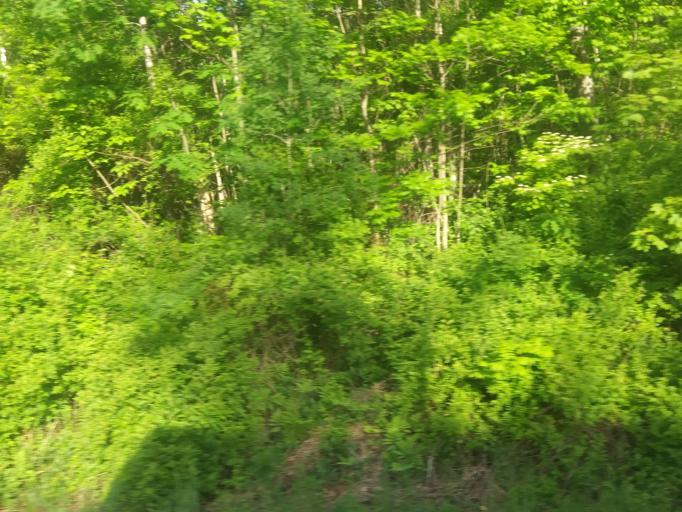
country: US
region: Massachusetts
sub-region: Franklin County
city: Shelburne Falls
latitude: 42.5977
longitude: -72.7443
